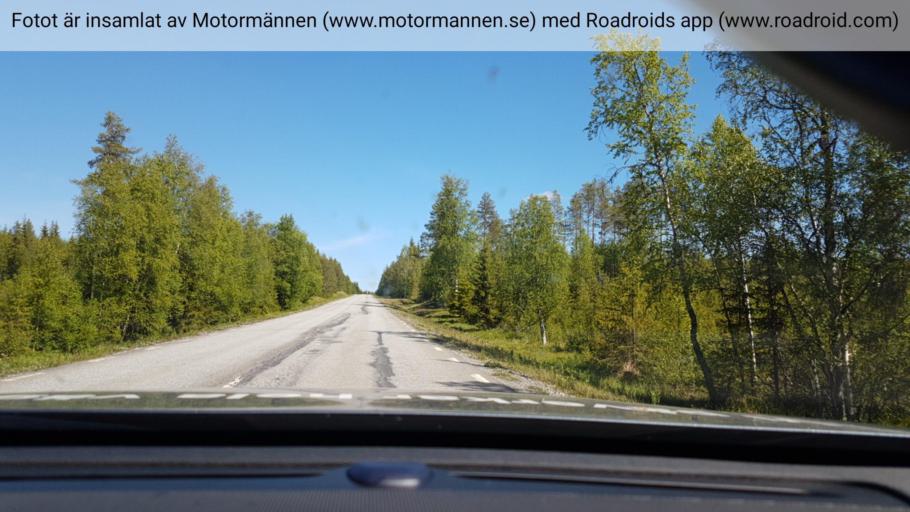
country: SE
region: Vaesterbotten
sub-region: Vilhelmina Kommun
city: Vilhelmina
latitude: 64.6305
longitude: 16.8080
